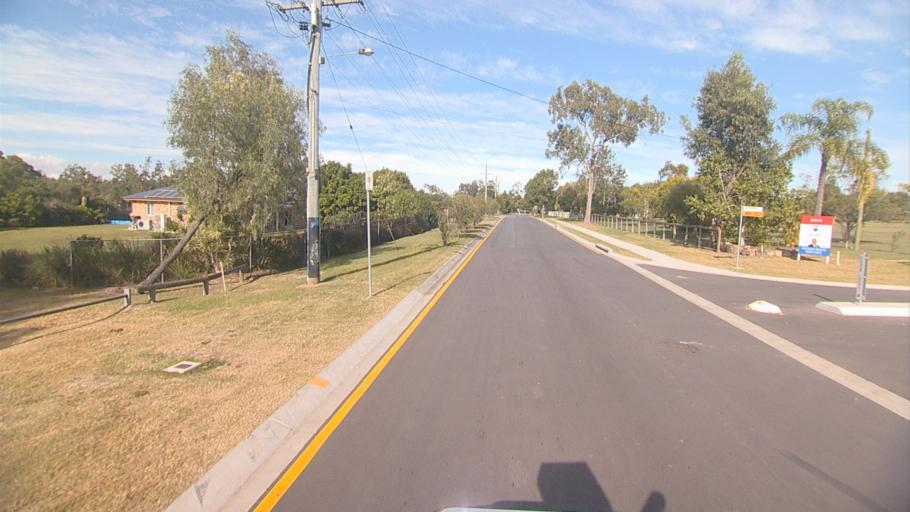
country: AU
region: Queensland
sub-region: Brisbane
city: Forest Lake
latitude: -27.6566
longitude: 152.9952
